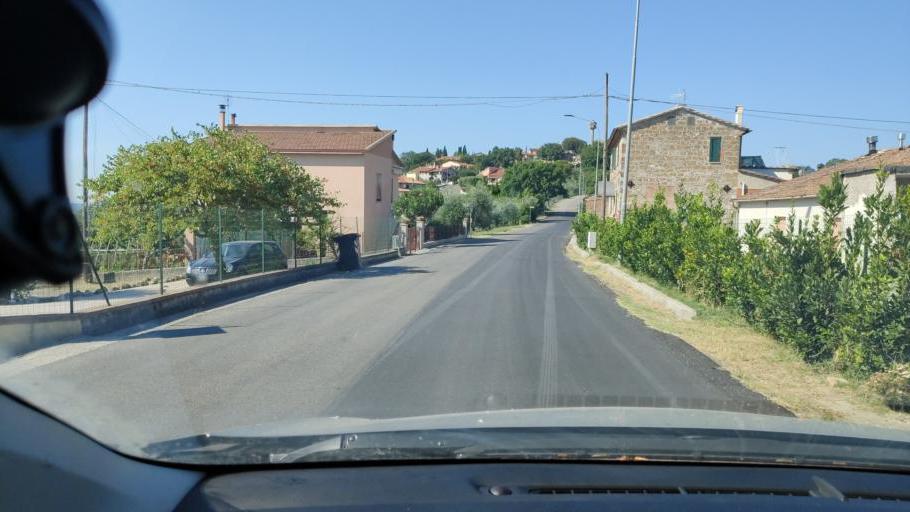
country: IT
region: Umbria
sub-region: Provincia di Terni
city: Fornole
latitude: 42.5176
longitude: 12.4320
